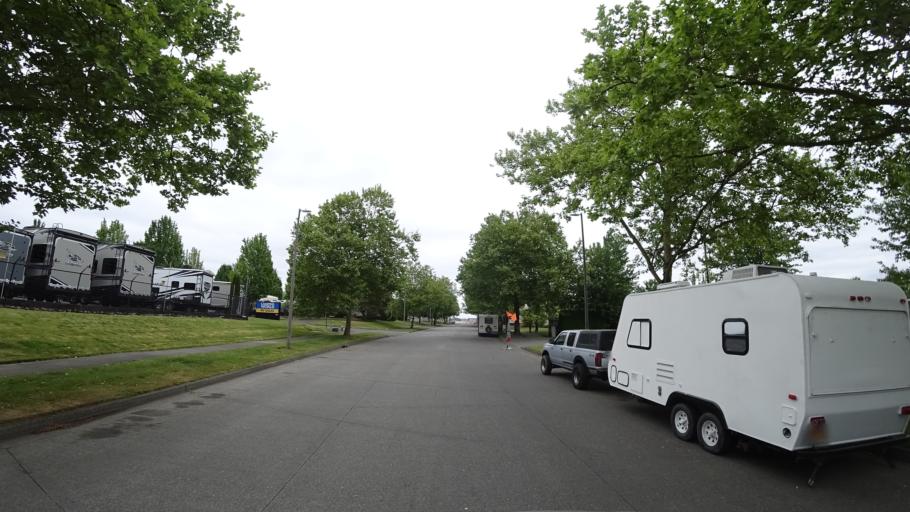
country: US
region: Oregon
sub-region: Washington County
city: Aloha
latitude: 45.4968
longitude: -122.9156
